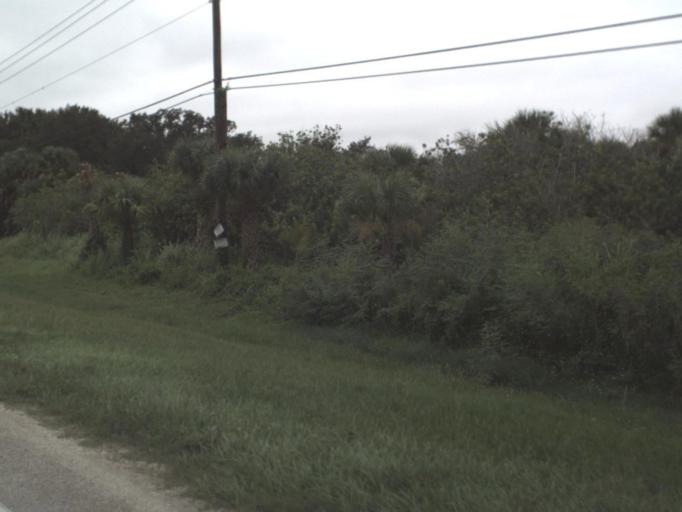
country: US
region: Florida
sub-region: Manatee County
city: Memphis
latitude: 27.6113
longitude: -82.5398
